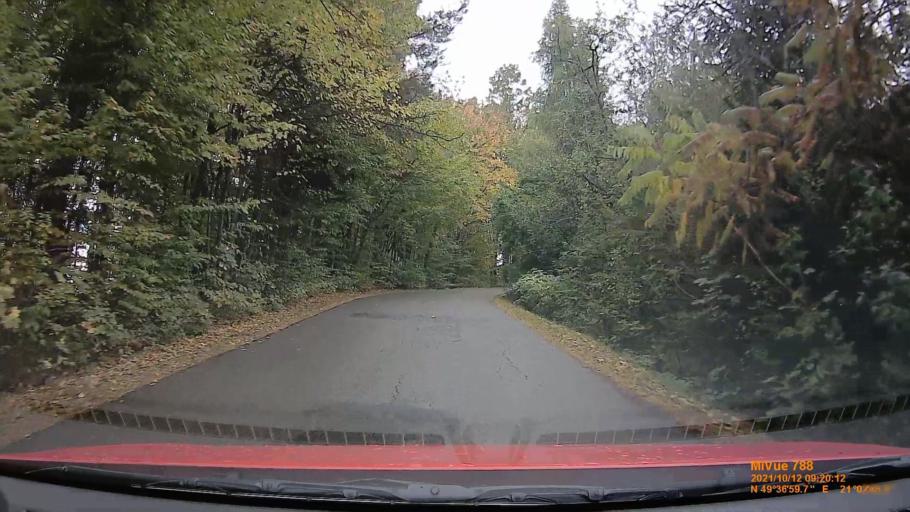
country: PL
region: Lesser Poland Voivodeship
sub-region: Powiat gorlicki
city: Ropa
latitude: 49.6165
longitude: 21.0457
